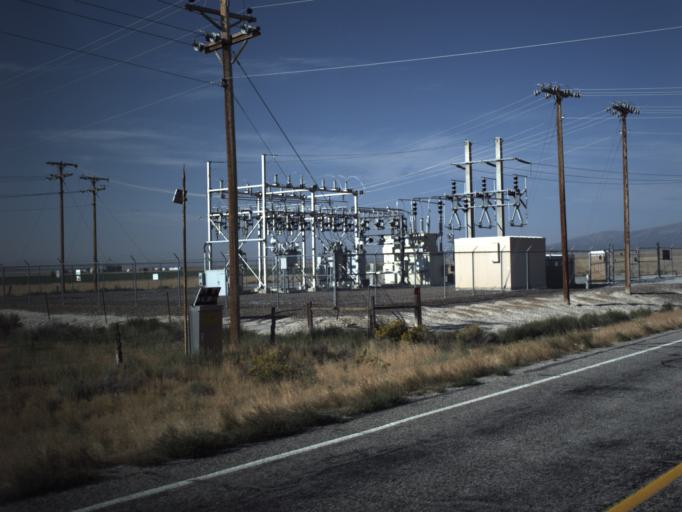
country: US
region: Idaho
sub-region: Oneida County
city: Malad City
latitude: 41.9663
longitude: -112.9435
